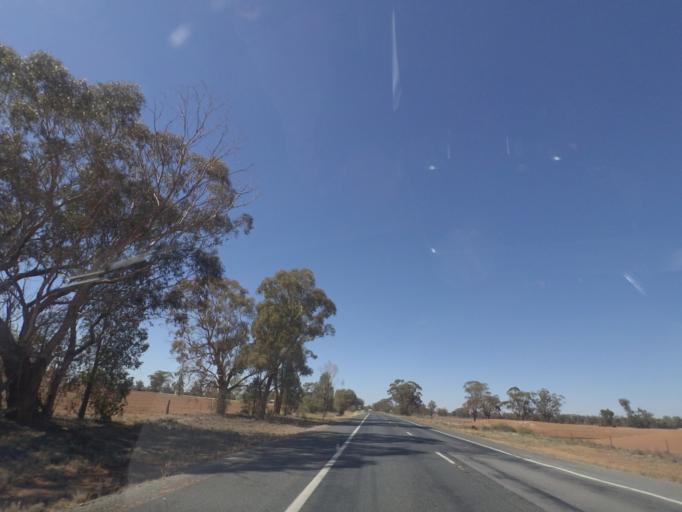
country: AU
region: New South Wales
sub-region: Bland
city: West Wyalong
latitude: -34.1905
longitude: 147.1118
